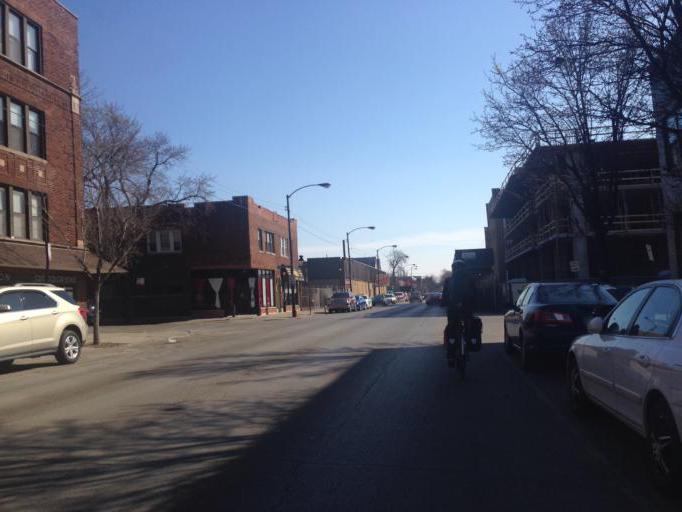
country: US
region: Illinois
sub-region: Cook County
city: Lincolnwood
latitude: 41.9561
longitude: -87.7081
